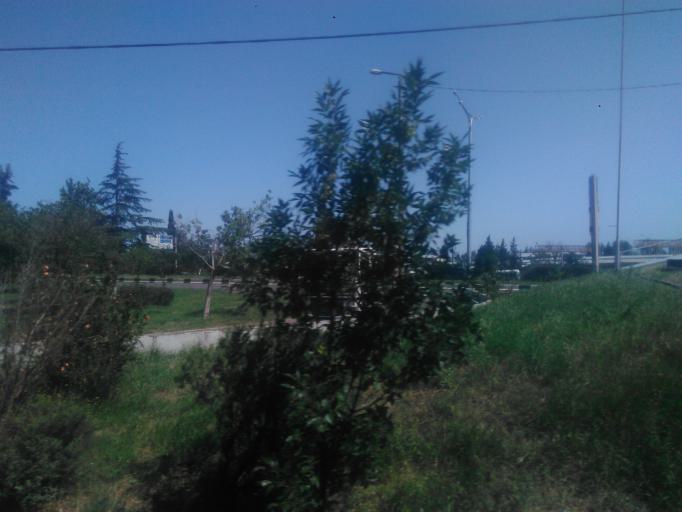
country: GE
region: T'bilisi
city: Tbilisi
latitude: 41.6872
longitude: 44.8927
